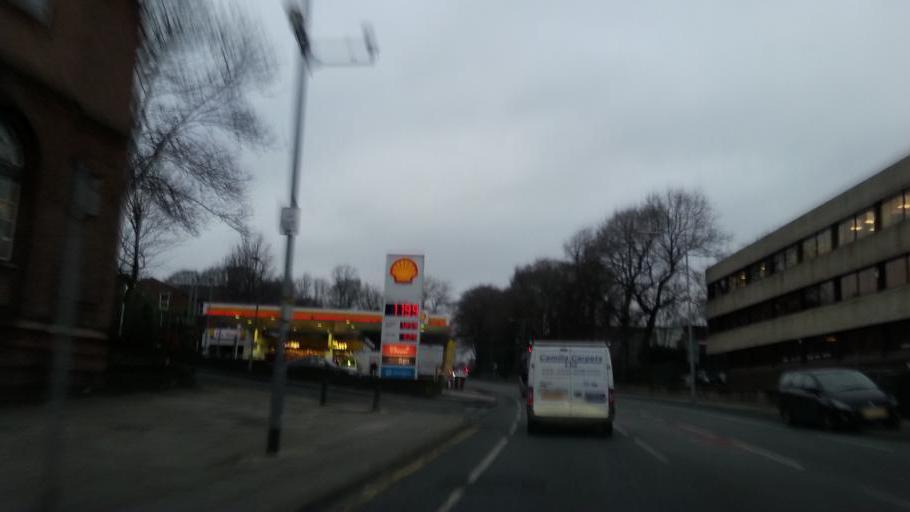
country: GB
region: England
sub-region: Borough of Bury
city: Prestwich
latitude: 53.5201
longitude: -2.2725
